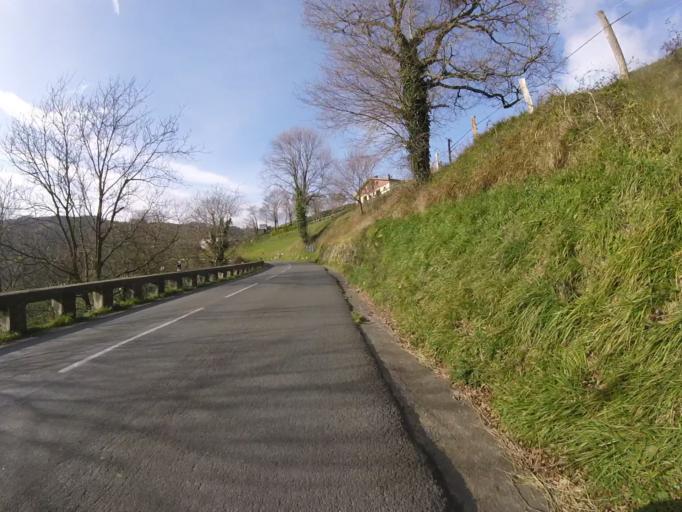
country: ES
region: Basque Country
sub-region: Provincia de Guipuzcoa
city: Larraul
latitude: 43.2036
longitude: -2.1292
